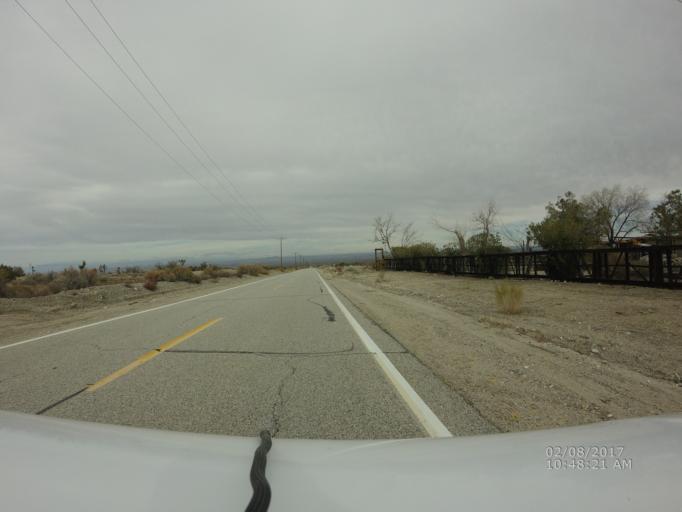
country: US
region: California
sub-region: San Bernardino County
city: Pinon Hills
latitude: 34.4629
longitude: -117.7650
